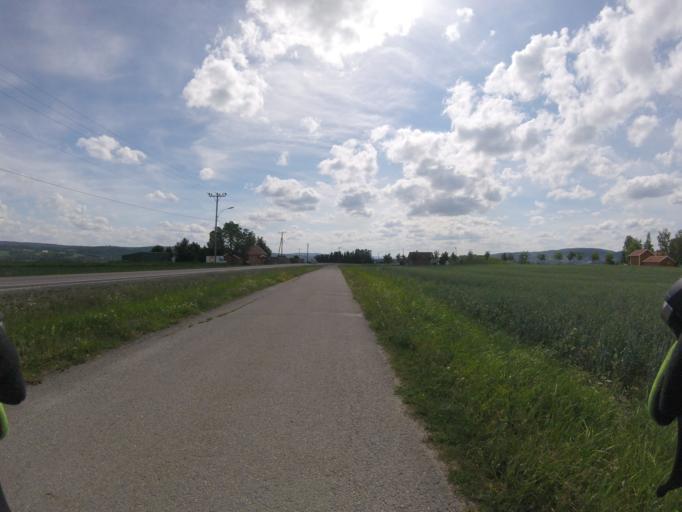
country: NO
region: Akershus
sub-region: Skedsmo
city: Lillestrom
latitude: 59.9805
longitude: 11.0538
